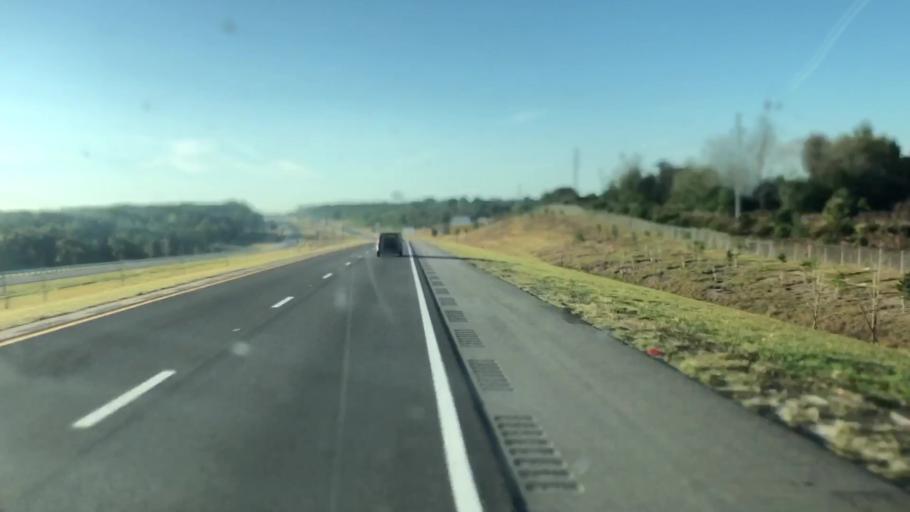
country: US
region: Florida
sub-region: Orange County
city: Zellwood
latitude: 28.7261
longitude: -81.5635
